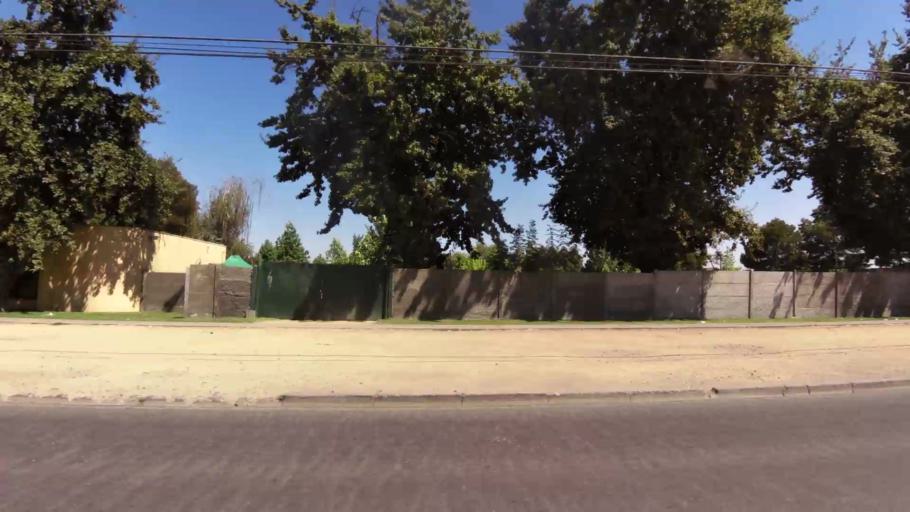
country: CL
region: Maule
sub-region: Provincia de Curico
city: Curico
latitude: -34.9749
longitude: -71.2319
